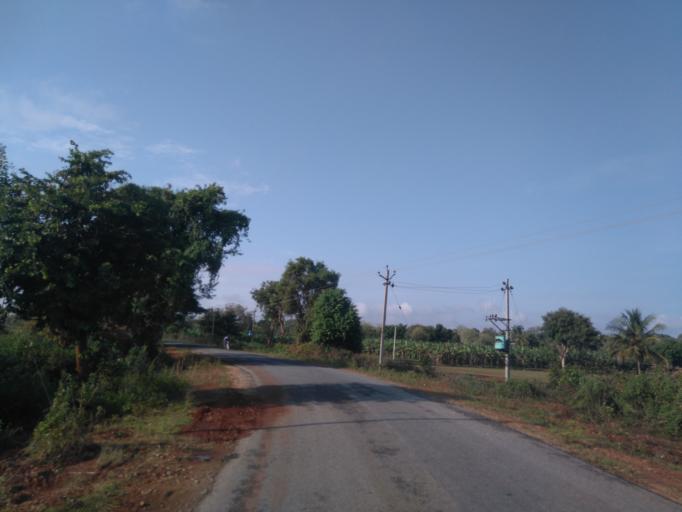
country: IN
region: Karnataka
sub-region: Mandya
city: Malavalli
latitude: 12.3134
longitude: 77.0717
